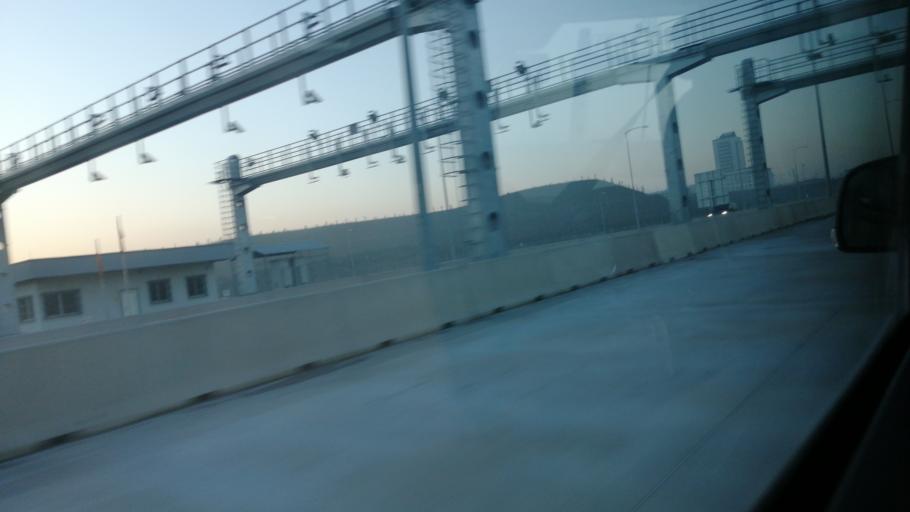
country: TR
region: Kocaeli
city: Tavsanli
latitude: 40.7852
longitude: 29.5158
